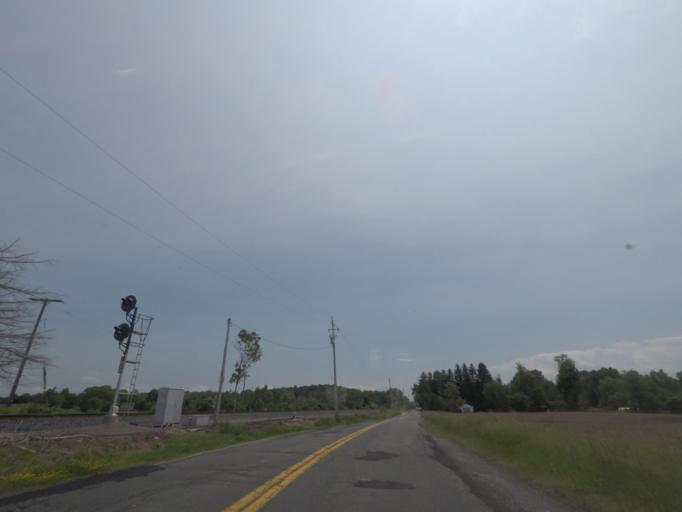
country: US
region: New York
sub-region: Rensselaer County
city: Castleton-on-Hudson
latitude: 42.4947
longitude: -73.6988
